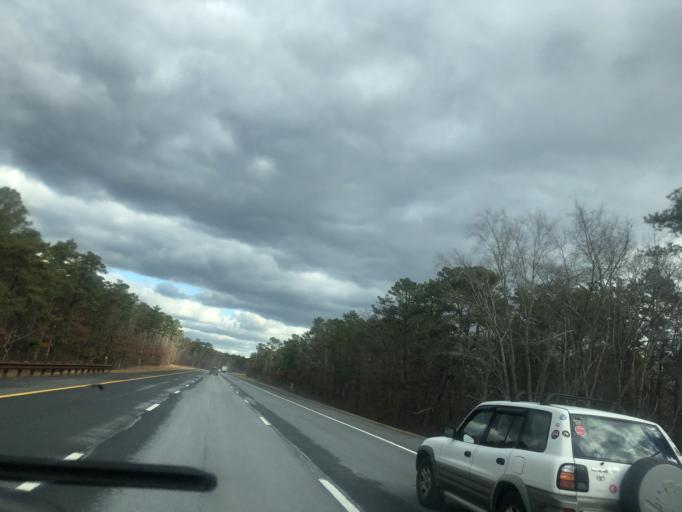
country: US
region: New Jersey
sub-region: Ocean County
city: Tuckerton
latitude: 39.6382
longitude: -74.3698
